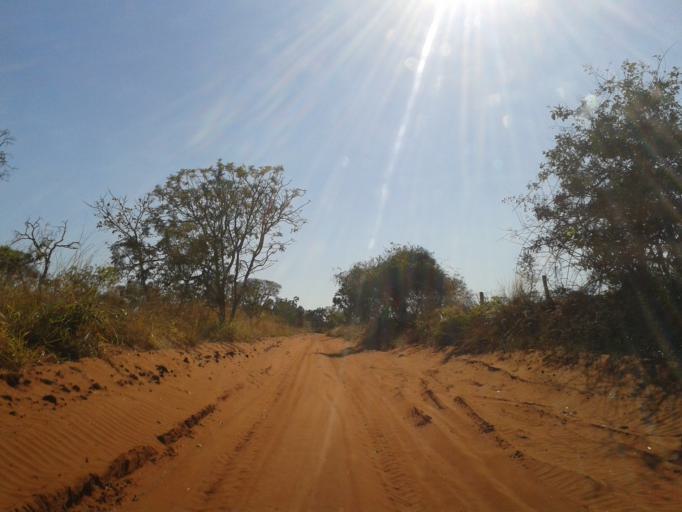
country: BR
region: Minas Gerais
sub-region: Ituiutaba
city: Ituiutaba
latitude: -19.0341
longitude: -49.3232
